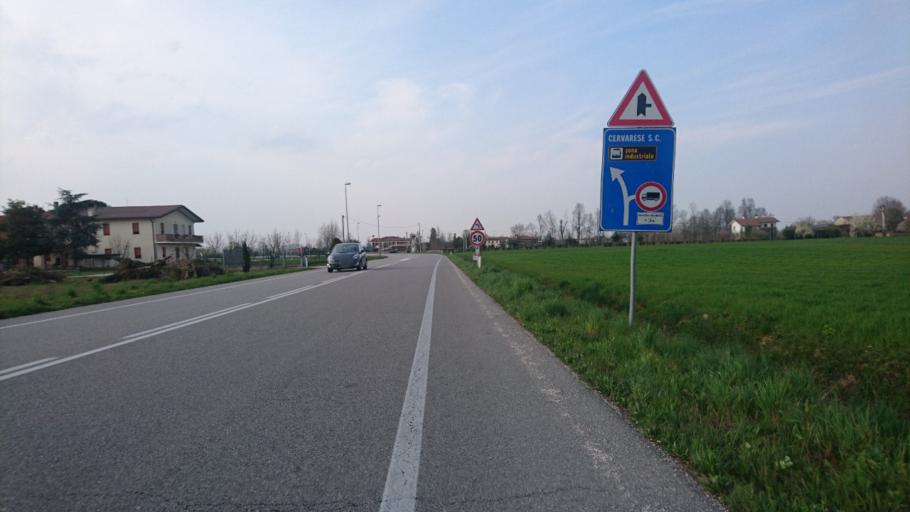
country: IT
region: Veneto
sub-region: Provincia di Padova
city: San Biagio
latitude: 45.3820
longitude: 11.7296
